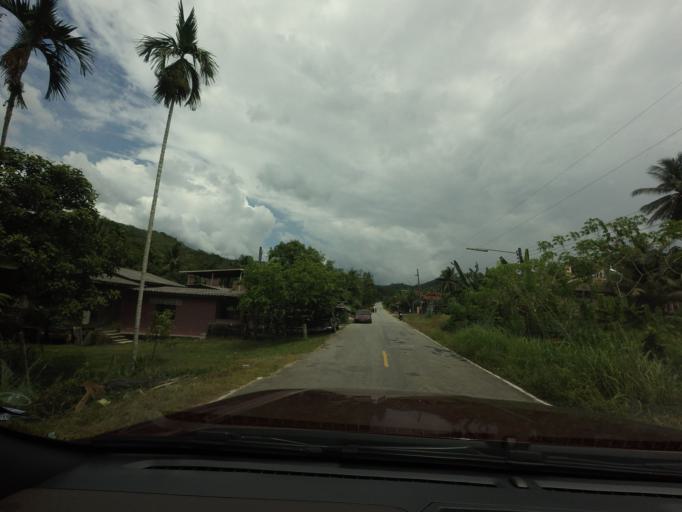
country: TH
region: Narathiwat
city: Chanae
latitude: 6.0391
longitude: 101.6925
